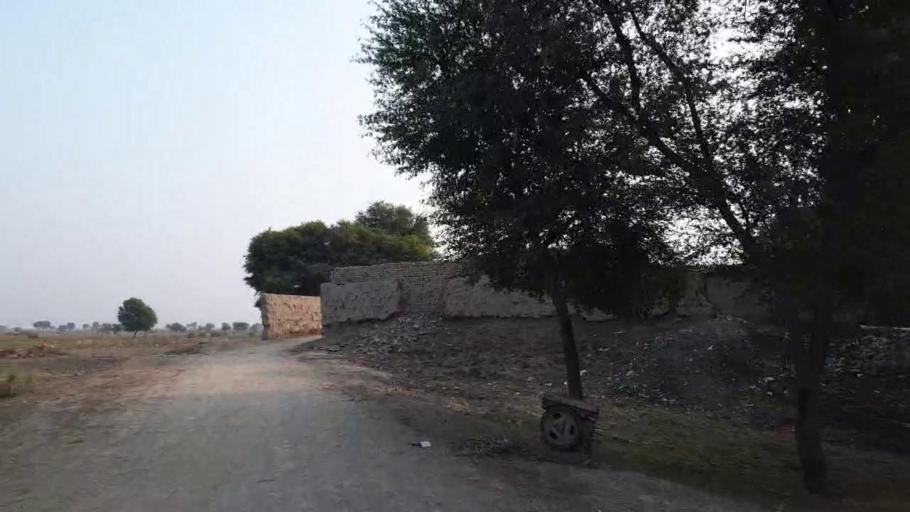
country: PK
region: Sindh
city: Bhan
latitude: 26.4930
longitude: 67.7379
